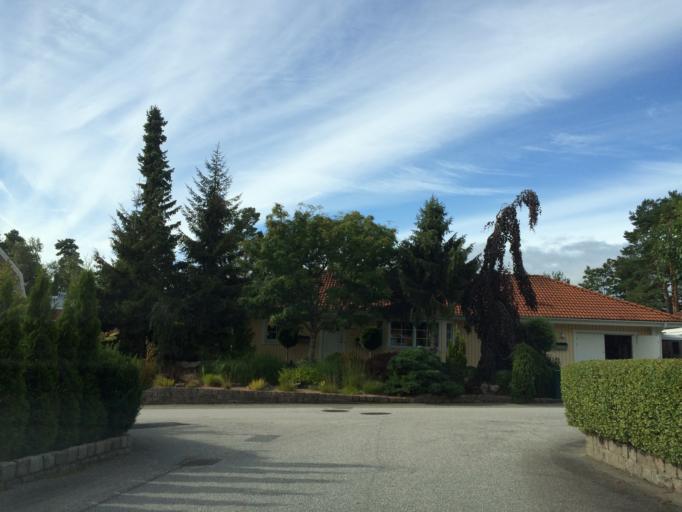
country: SE
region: Vaestra Goetaland
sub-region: Trollhattan
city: Trollhattan
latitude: 58.3243
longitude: 12.2734
